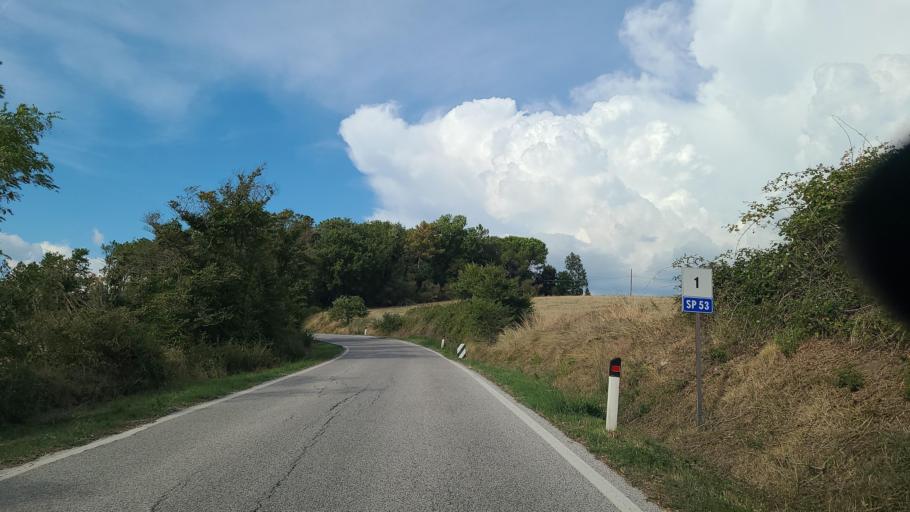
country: IT
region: Tuscany
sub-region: Provincia di Siena
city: San Gimignano
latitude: 43.4118
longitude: 10.9773
